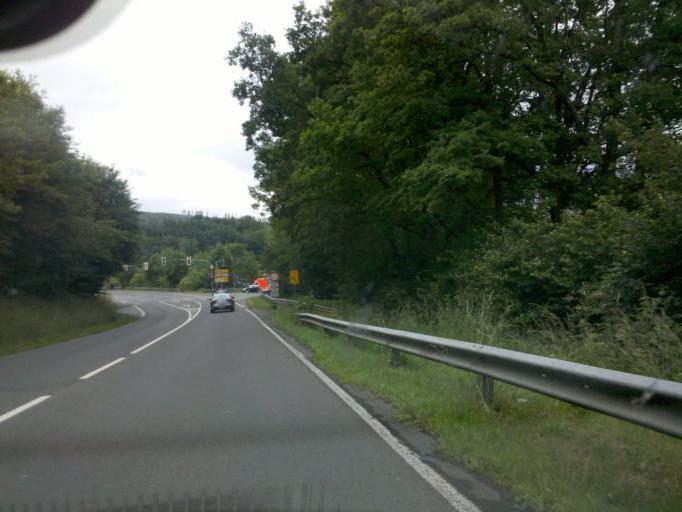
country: DE
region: North Rhine-Westphalia
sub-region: Regierungsbezirk Arnsberg
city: Olpe
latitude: 51.0414
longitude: 7.8623
